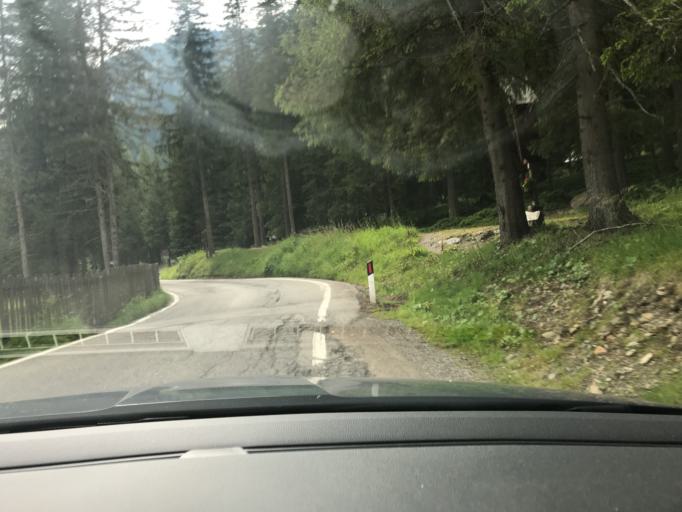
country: IT
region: Trentino-Alto Adige
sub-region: Bolzano
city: San Martino
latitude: 46.8838
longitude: 12.1596
